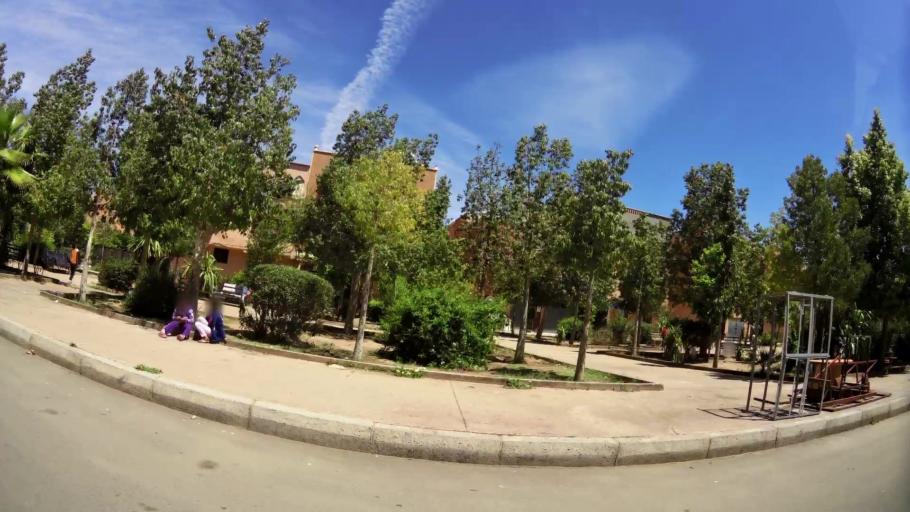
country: MA
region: Marrakech-Tensift-Al Haouz
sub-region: Marrakech
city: Marrakesh
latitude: 31.6388
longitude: -8.0460
